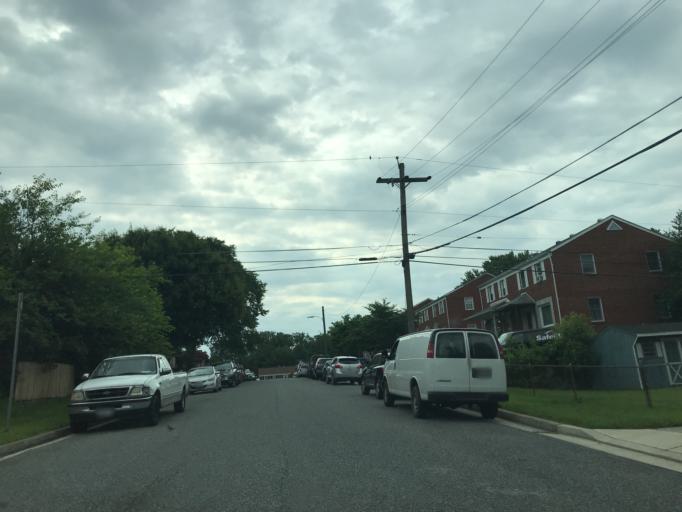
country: US
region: Maryland
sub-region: Baltimore County
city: Overlea
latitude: 39.3602
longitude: -76.5119
